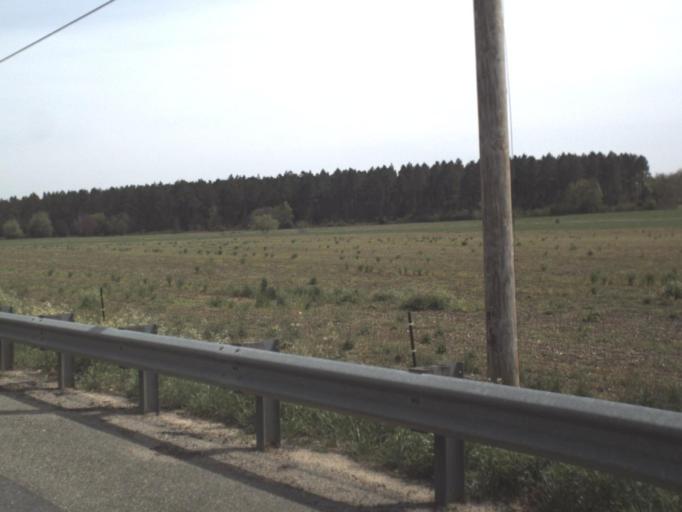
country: US
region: Florida
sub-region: Jackson County
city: Graceville
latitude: 30.9524
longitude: -85.4202
